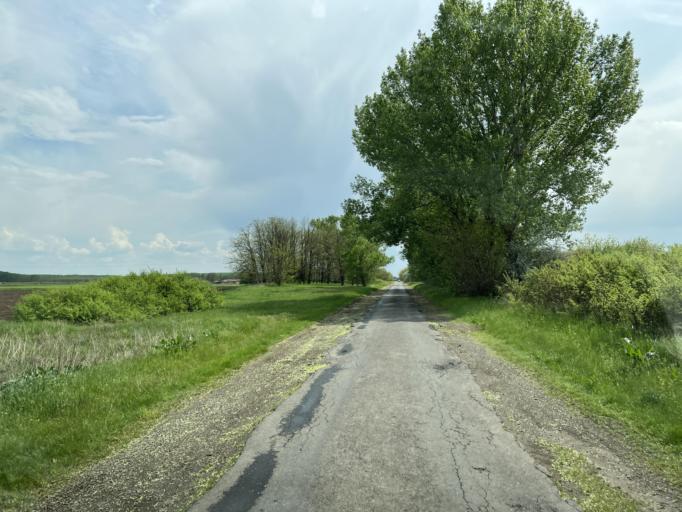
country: HU
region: Pest
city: Nagykoros
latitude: 46.9876
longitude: 19.8045
